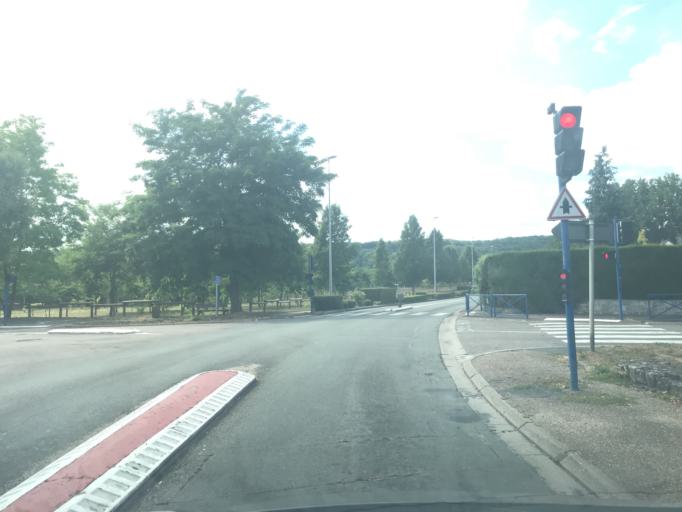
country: FR
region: Haute-Normandie
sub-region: Departement de l'Eure
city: Aubevoye
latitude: 49.1704
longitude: 1.3451
